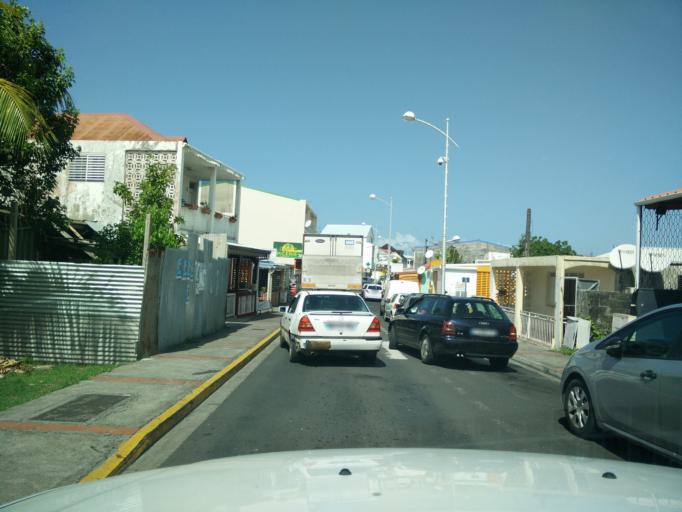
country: GP
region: Guadeloupe
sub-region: Guadeloupe
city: Le Gosier
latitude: 16.2059
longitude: -61.4879
